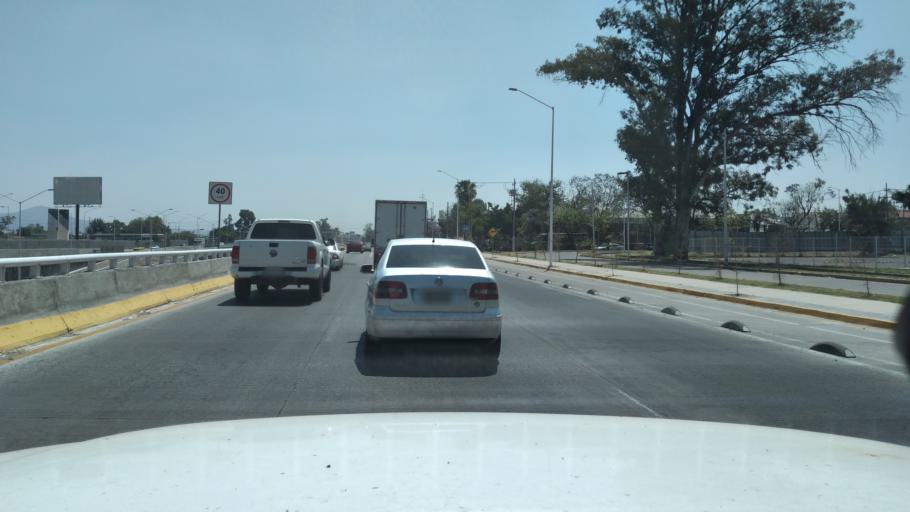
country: MX
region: Jalisco
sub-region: Zapopan
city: Zapopan
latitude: 20.7384
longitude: -103.3797
